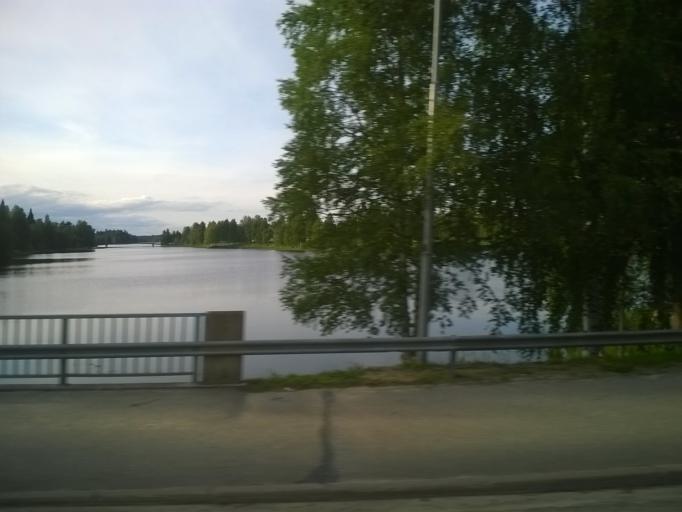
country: FI
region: Kainuu
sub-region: Kajaani
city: Sotkamo
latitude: 64.1311
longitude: 28.3968
